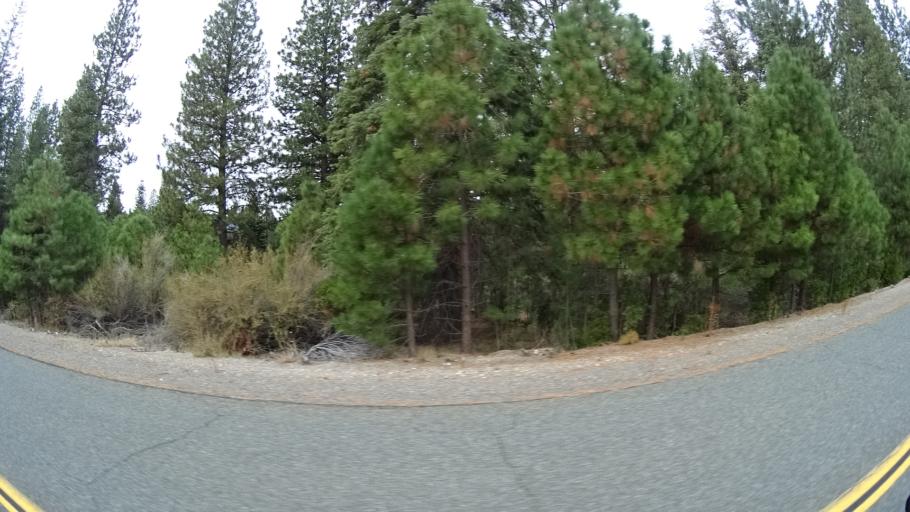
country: US
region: California
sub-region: Siskiyou County
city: Weed
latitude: 41.4111
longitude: -122.3716
